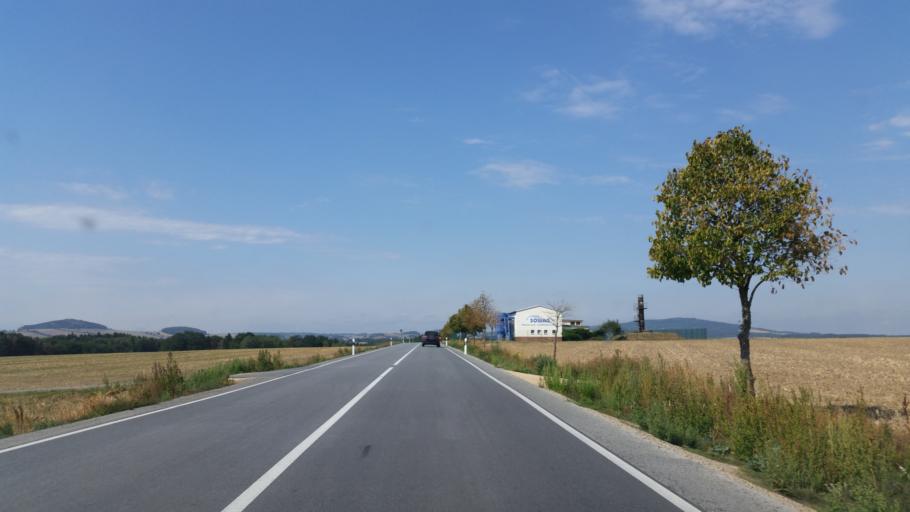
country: DE
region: Saxony
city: Grosshennersdorf
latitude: 50.9804
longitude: 14.7712
